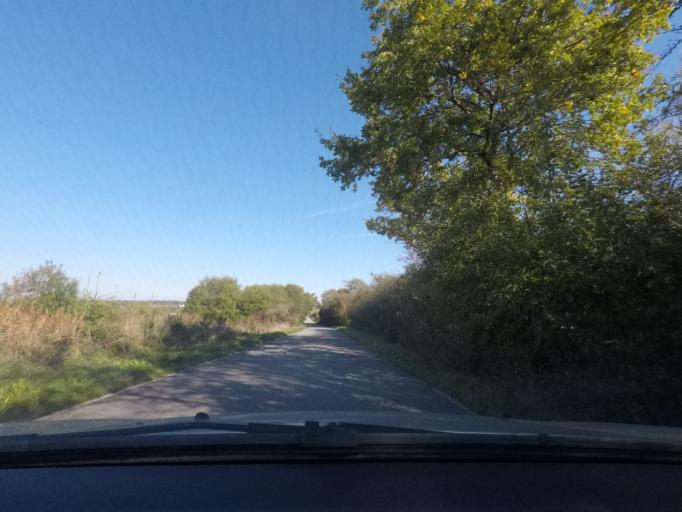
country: BE
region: Wallonia
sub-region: Province du Luxembourg
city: Etalle
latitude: 49.7129
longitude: 5.5661
